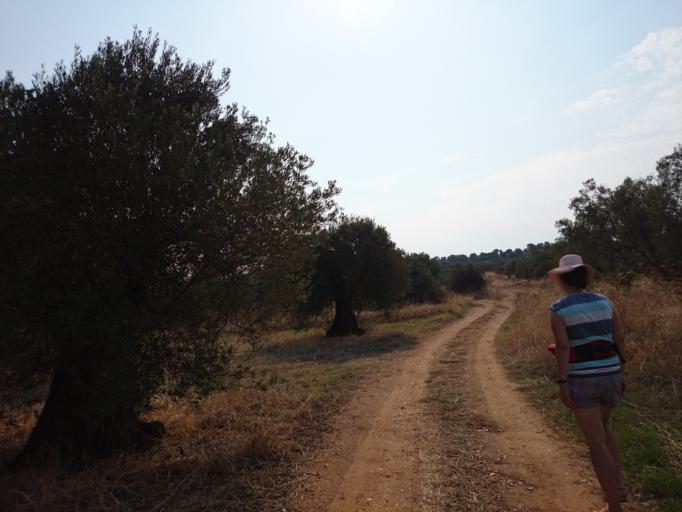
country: GR
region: Central Macedonia
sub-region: Nomos Chalkidikis
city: Nea Moudhania
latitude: 40.2538
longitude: 23.2677
